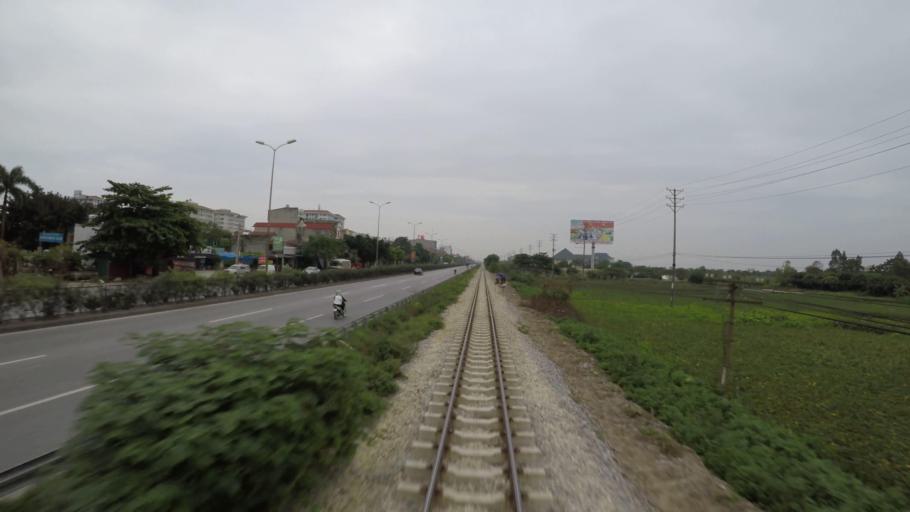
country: VN
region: Hung Yen
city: Nhu Quynh
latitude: 20.9849
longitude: 105.9782
